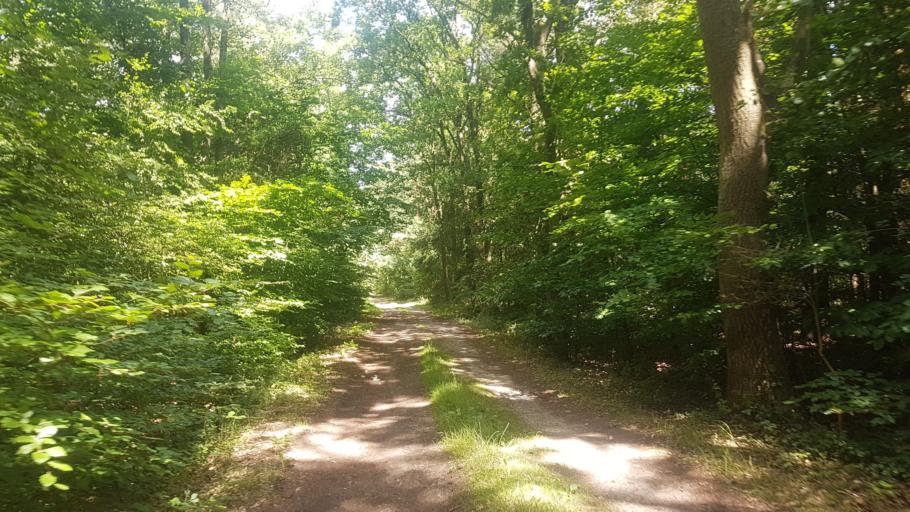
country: DE
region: Lower Saxony
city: Bleckede
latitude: 53.2713
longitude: 10.7766
